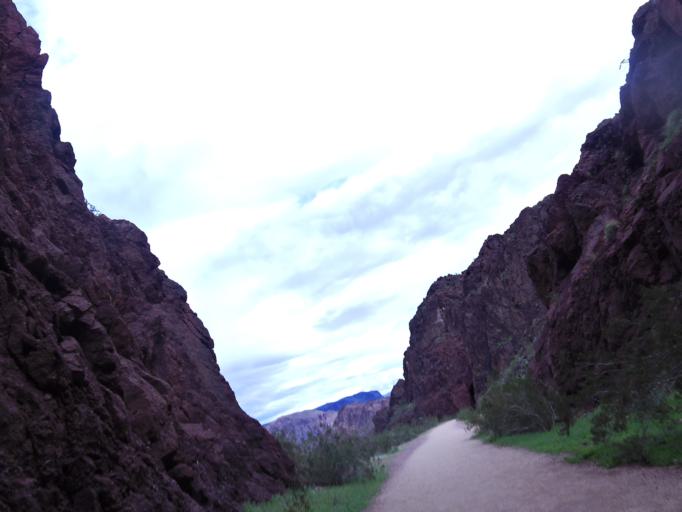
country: US
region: Nevada
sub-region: Clark County
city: Boulder City
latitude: 36.0161
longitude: -114.7676
